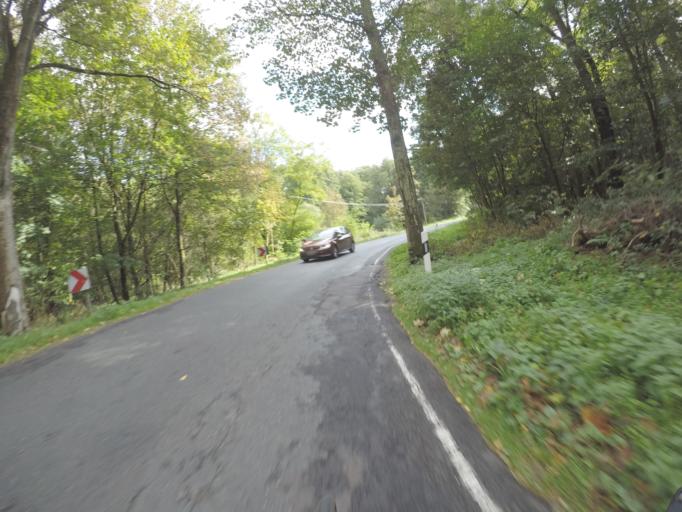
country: DE
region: Brandenburg
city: Strausberg
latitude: 52.6049
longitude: 13.8327
